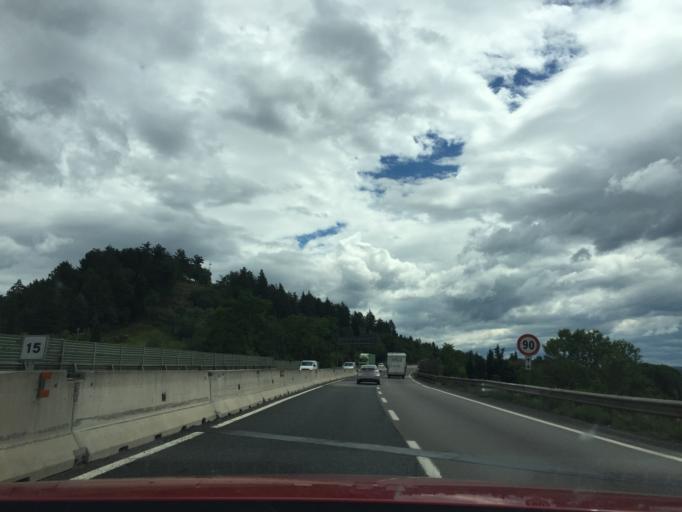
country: IT
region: Tuscany
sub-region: Province of Florence
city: Ginestra Fiorentina
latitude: 43.7123
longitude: 11.0598
